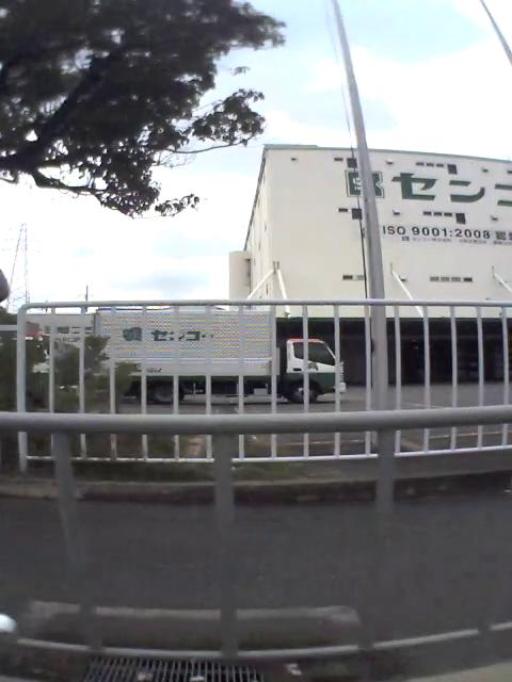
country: JP
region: Osaka
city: Neyagawa
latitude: 34.7524
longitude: 135.6251
